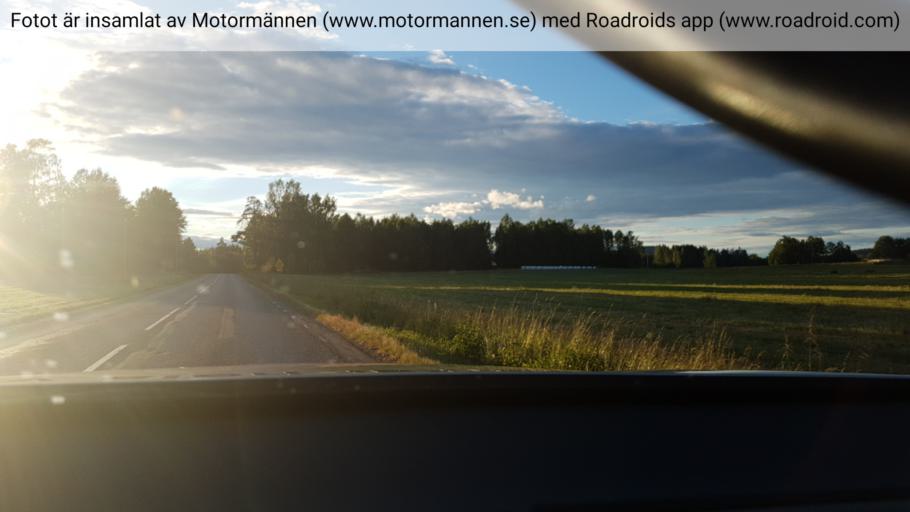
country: SE
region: Vaermland
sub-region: Torsby Kommun
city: Torsby
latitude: 60.0600
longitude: 13.1005
